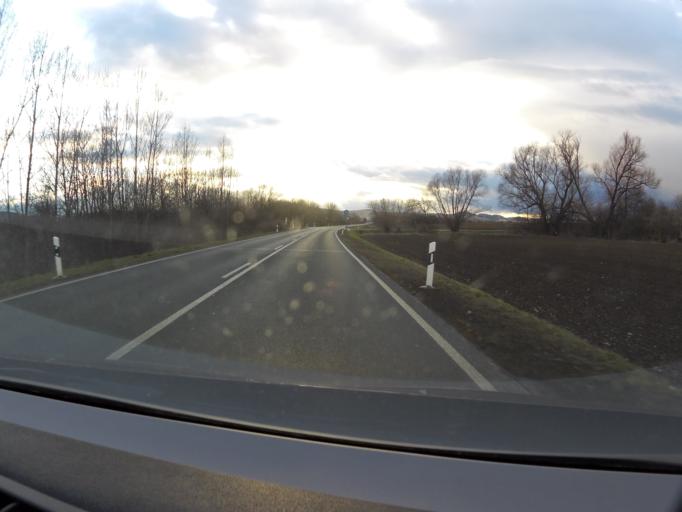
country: DE
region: Thuringia
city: Dornheim
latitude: 50.8507
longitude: 11.0014
